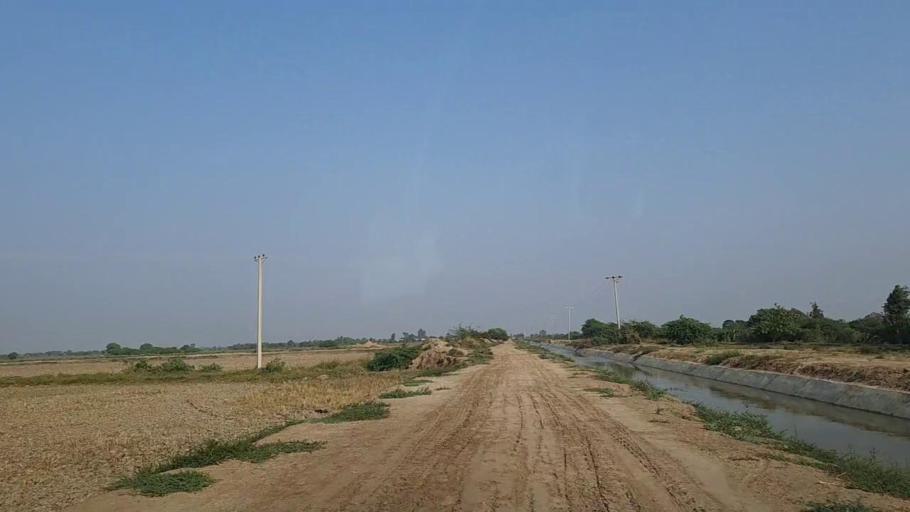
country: PK
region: Sindh
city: Mirpur Sakro
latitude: 24.6155
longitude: 67.7232
